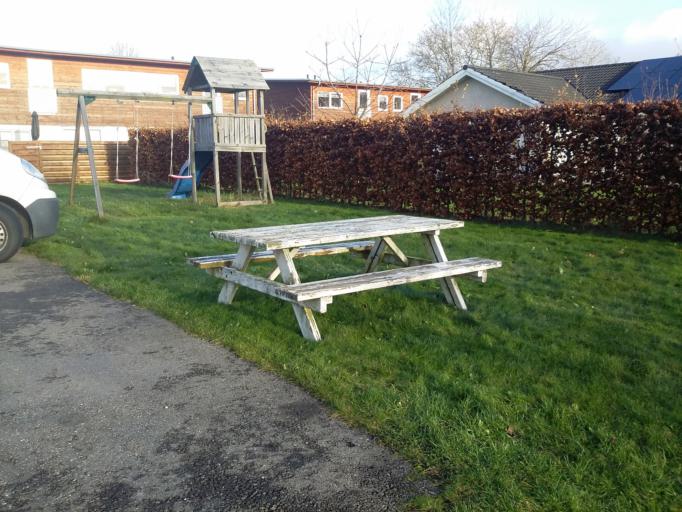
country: DK
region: Capital Region
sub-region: Frederikssund Kommune
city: Slangerup
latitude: 55.8418
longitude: 12.1717
